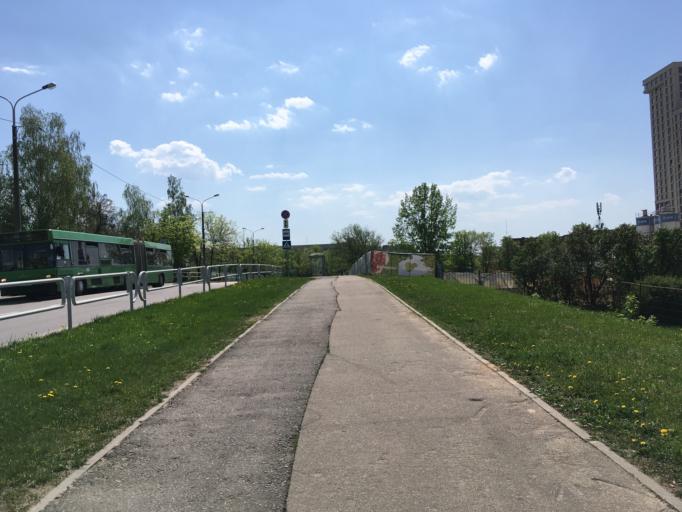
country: BY
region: Minsk
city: Minsk
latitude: 53.9236
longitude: 27.6279
